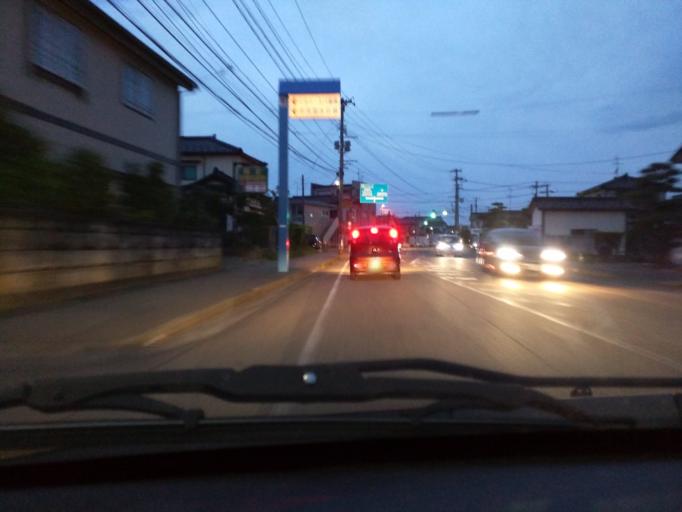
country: JP
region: Niigata
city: Kashiwazaki
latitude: 37.3689
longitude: 138.5738
